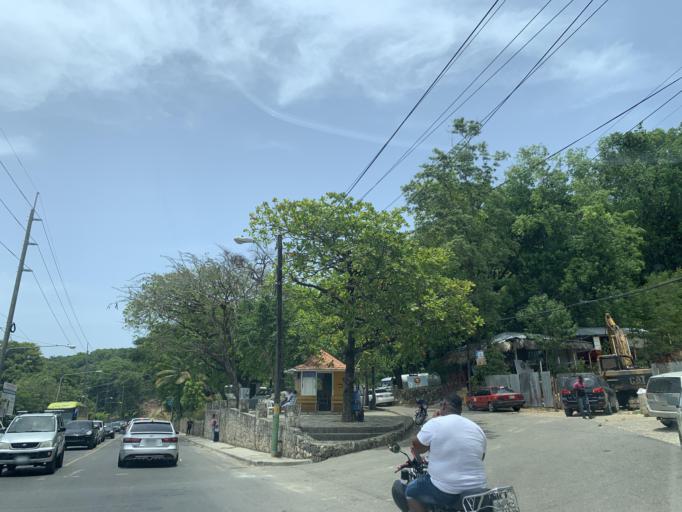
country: DO
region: Puerto Plata
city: Cabarete
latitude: 19.7527
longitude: -70.5190
